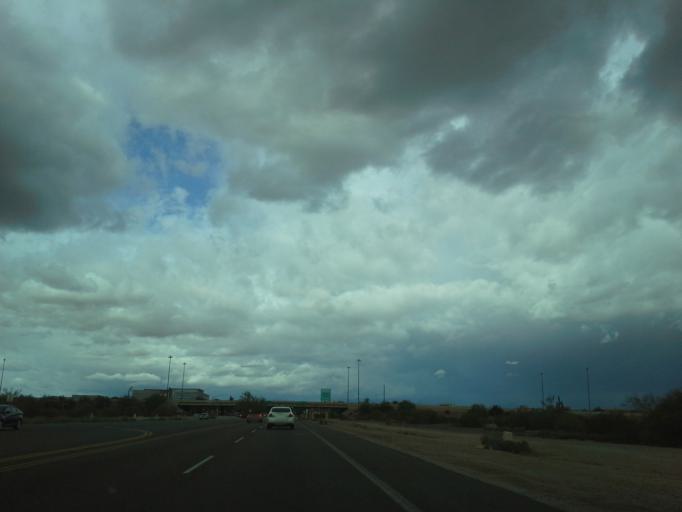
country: US
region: Arizona
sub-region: Maricopa County
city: Paradise Valley
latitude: 33.6692
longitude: -111.9773
